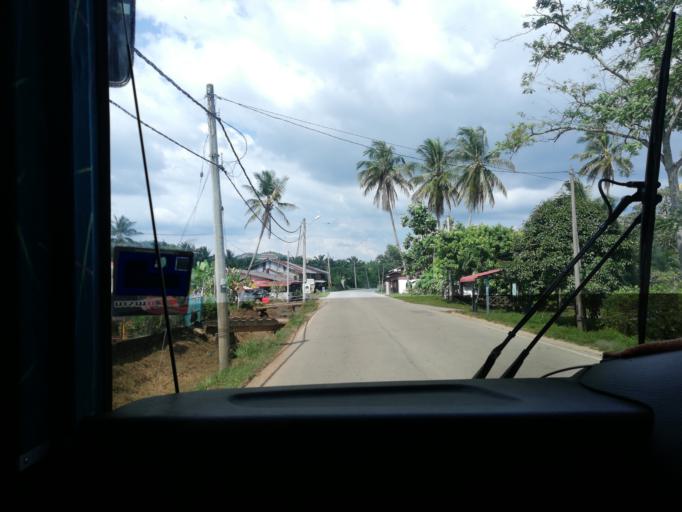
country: MY
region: Perak
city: Parit Buntar
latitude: 5.1179
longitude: 100.5613
